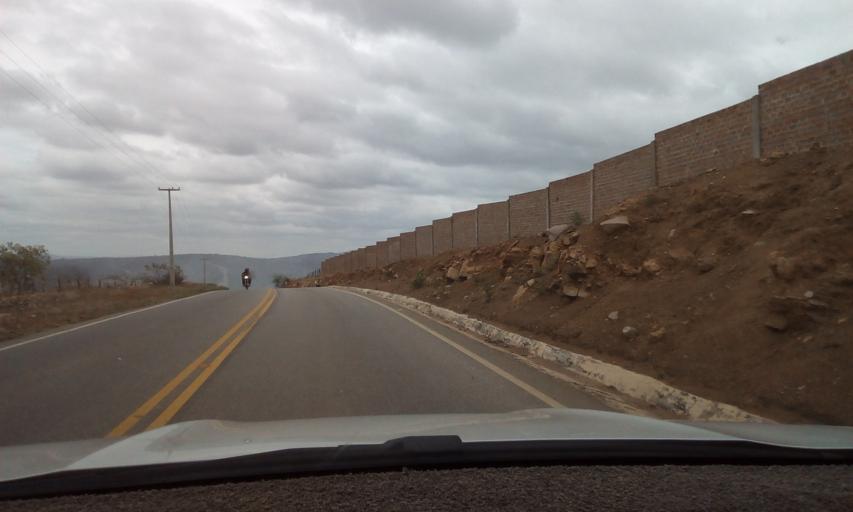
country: BR
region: Paraiba
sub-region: Picui
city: Picui
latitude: -6.5450
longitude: -36.2993
